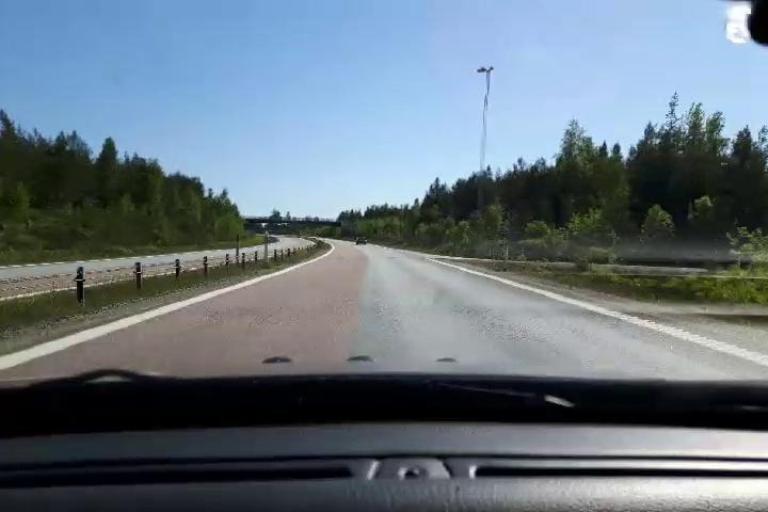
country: SE
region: Gaevleborg
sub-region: Soderhamns Kommun
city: Soderhamn
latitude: 61.3410
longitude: 17.0172
